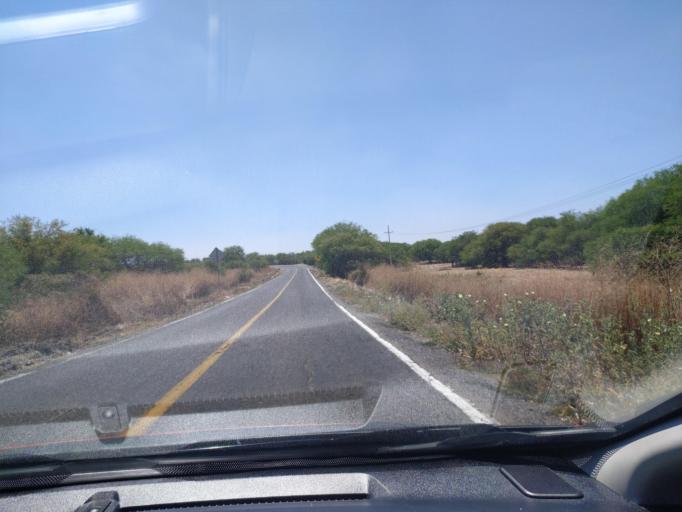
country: MX
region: Guanajuato
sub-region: San Francisco del Rincon
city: San Ignacio de Hidalgo
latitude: 20.7944
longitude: -101.8356
